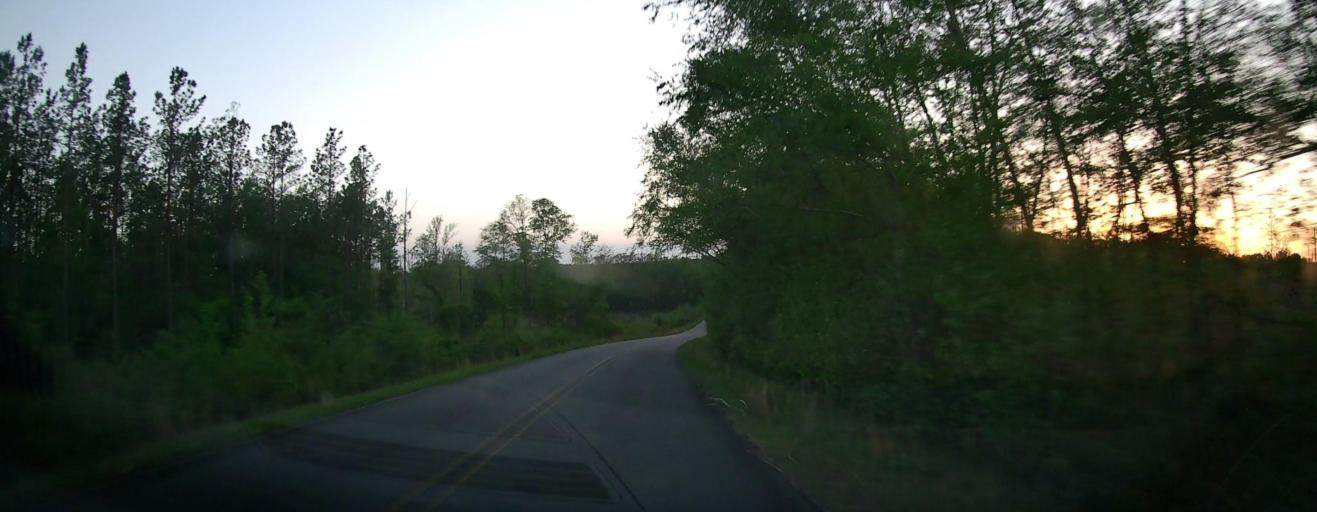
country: US
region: Georgia
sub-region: Marion County
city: Buena Vista
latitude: 32.2577
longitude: -84.5730
